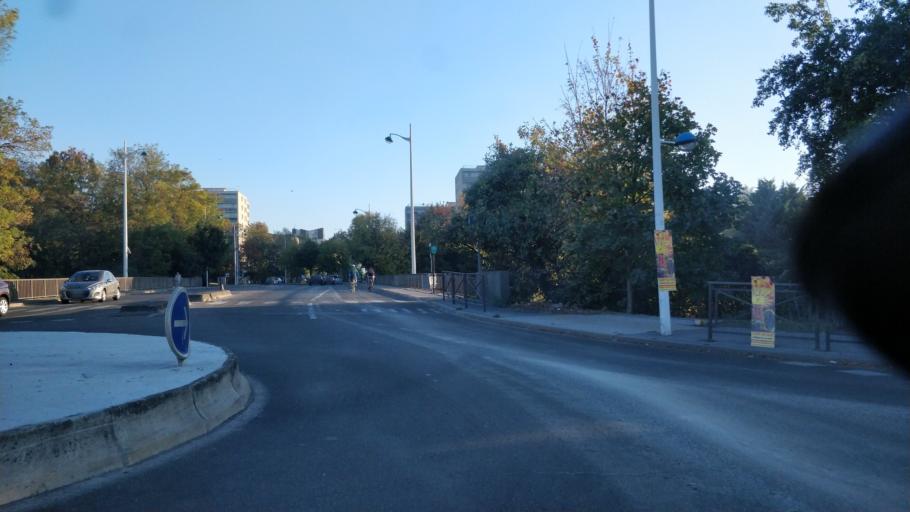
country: FR
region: Ile-de-France
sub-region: Departement de Seine-Saint-Denis
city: Gournay-sur-Marne
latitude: 48.8502
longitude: 2.5852
